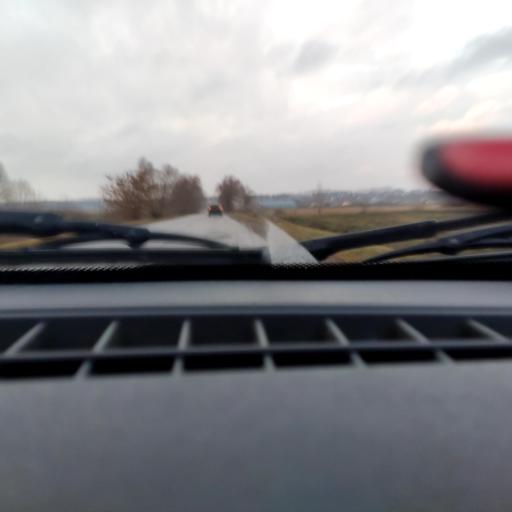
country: RU
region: Bashkortostan
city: Avdon
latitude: 54.5060
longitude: 55.8776
